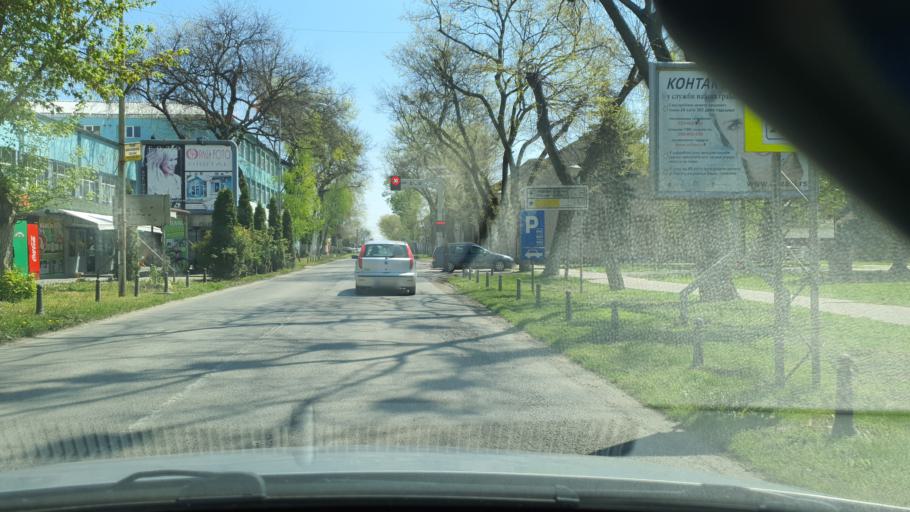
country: RS
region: Autonomna Pokrajina Vojvodina
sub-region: Zapadnobacki Okrug
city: Odzaci
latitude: 45.5060
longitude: 19.2595
